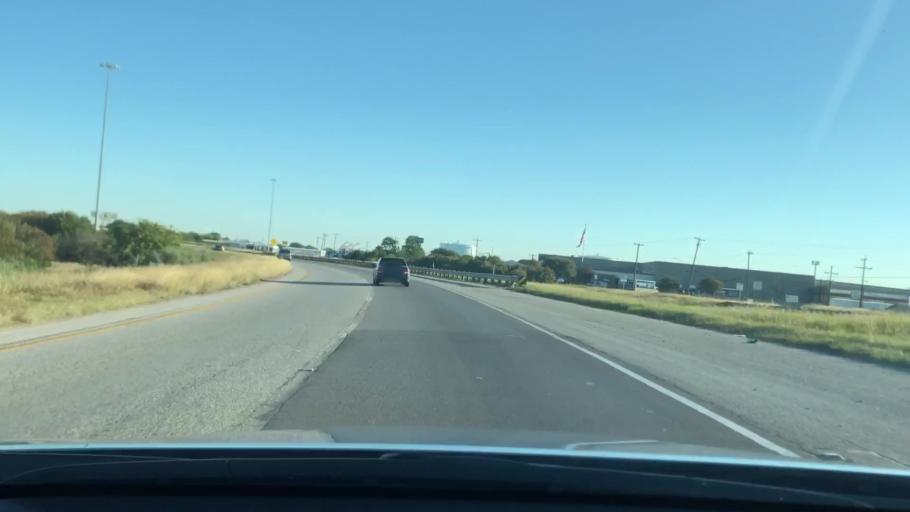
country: US
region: Texas
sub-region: Bexar County
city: Kirby
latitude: 29.4509
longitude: -98.4062
